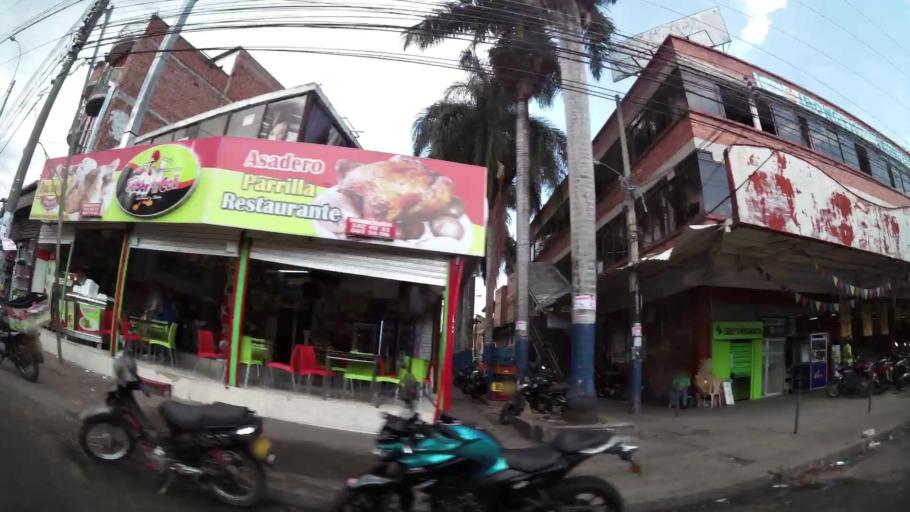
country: CO
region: Valle del Cauca
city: Cali
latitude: 3.4709
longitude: -76.4921
